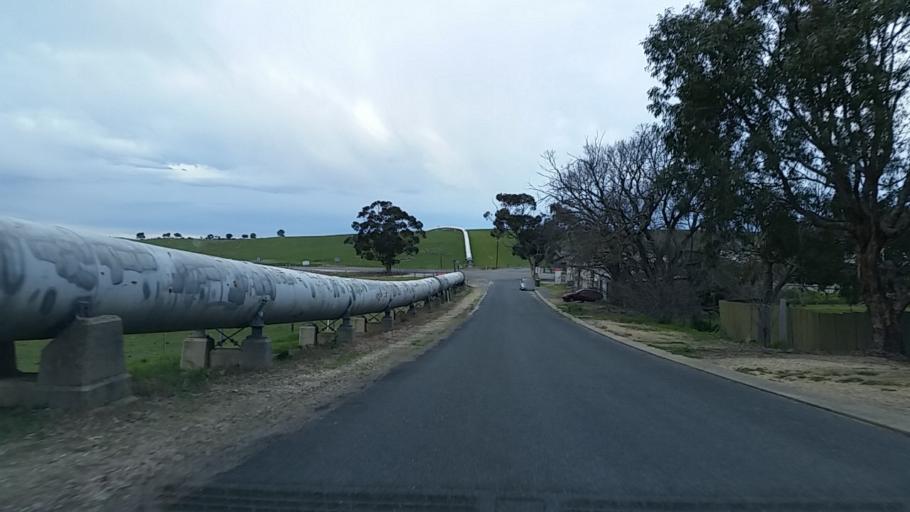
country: AU
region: South Australia
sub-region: Adelaide Hills
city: Birdwood
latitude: -34.8224
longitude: 139.0697
